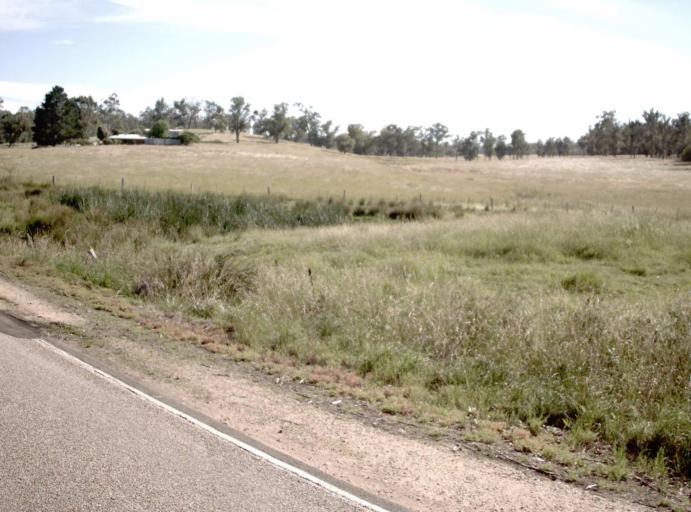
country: AU
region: Victoria
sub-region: East Gippsland
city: Lakes Entrance
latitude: -37.5406
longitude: 148.1483
